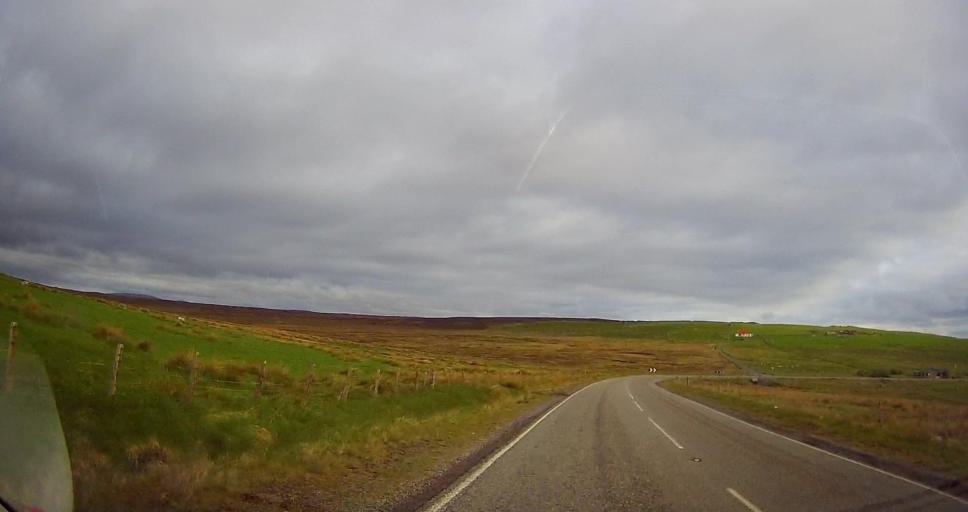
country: GB
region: Scotland
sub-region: Shetland Islands
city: Lerwick
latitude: 60.4645
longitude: -1.2118
